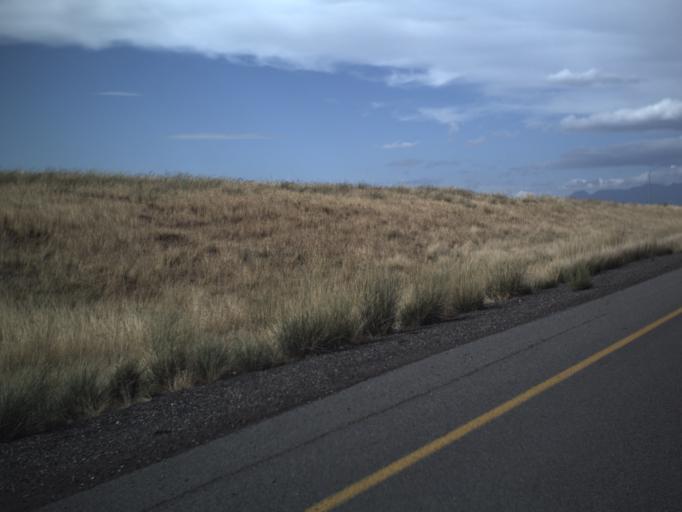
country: US
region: Utah
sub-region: Utah County
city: Santaquin
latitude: 39.9511
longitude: -111.8016
